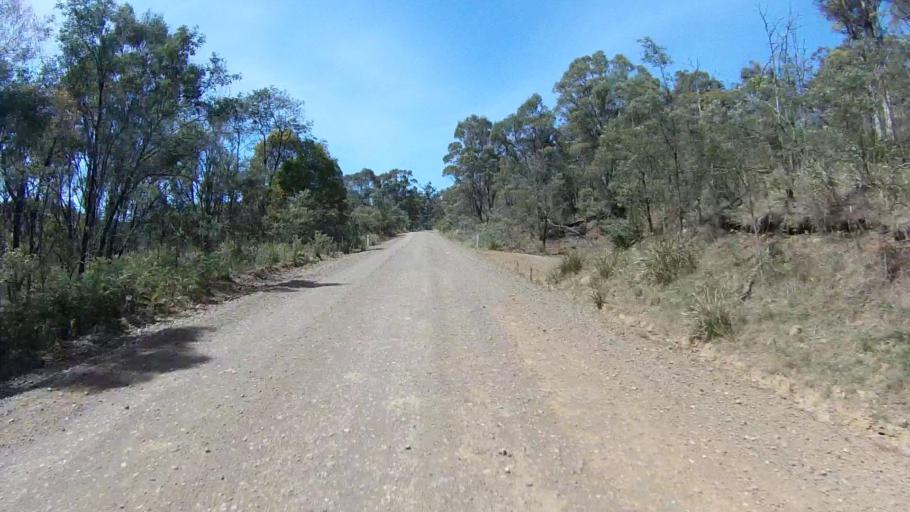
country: AU
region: Tasmania
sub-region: Sorell
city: Sorell
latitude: -42.6460
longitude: 147.7419
